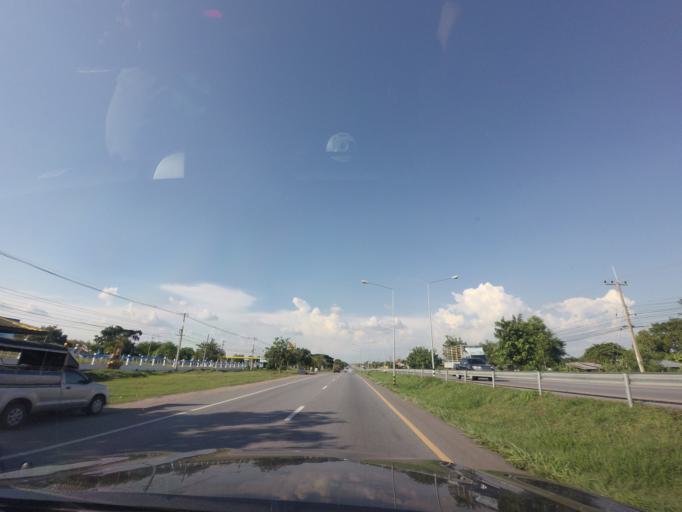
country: TH
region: Khon Kaen
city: Non Sila
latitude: 15.9781
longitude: 102.6950
